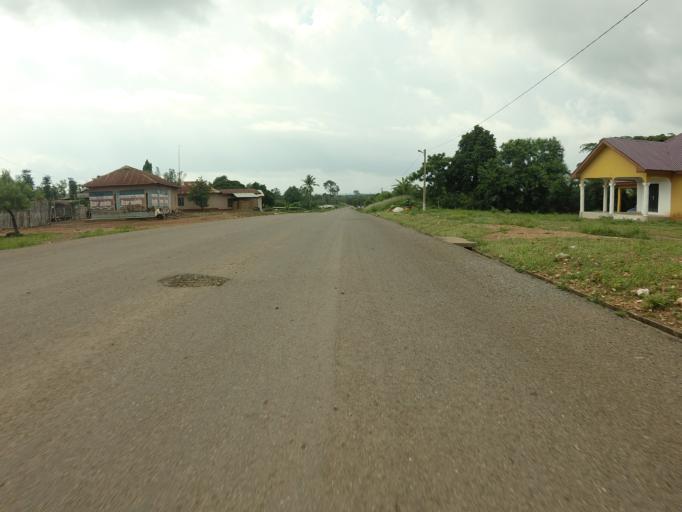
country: GH
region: Volta
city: Kpandu
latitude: 6.9528
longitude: 0.4582
